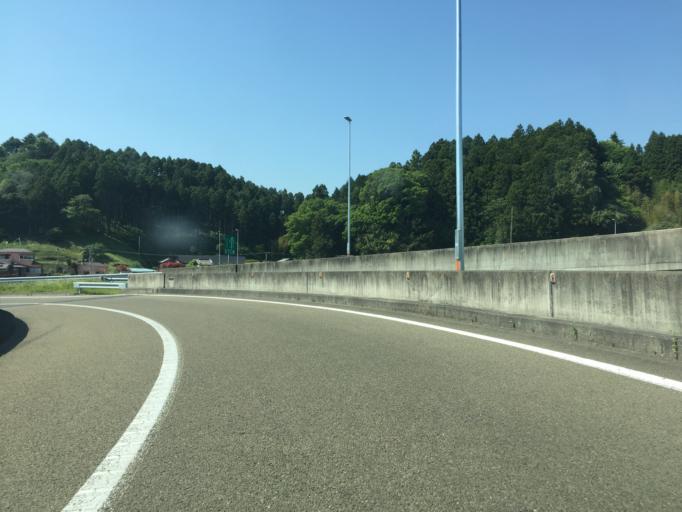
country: JP
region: Miyagi
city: Matsushima
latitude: 38.4013
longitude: 141.0714
